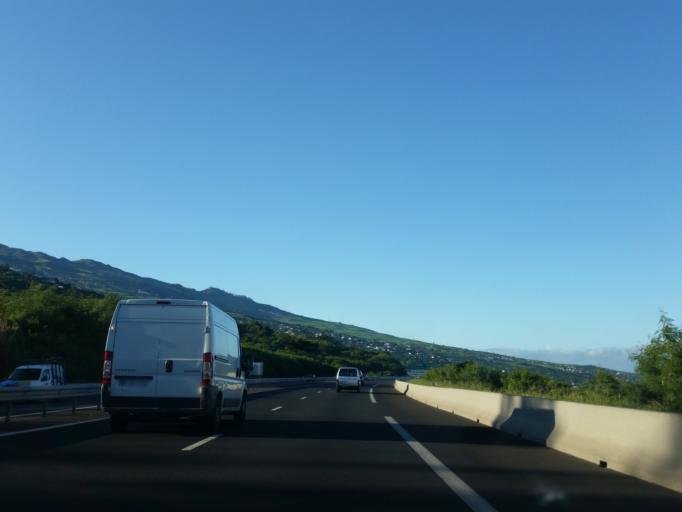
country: RE
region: Reunion
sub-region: Reunion
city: Saint-Leu
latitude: -21.1469
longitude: 55.2887
